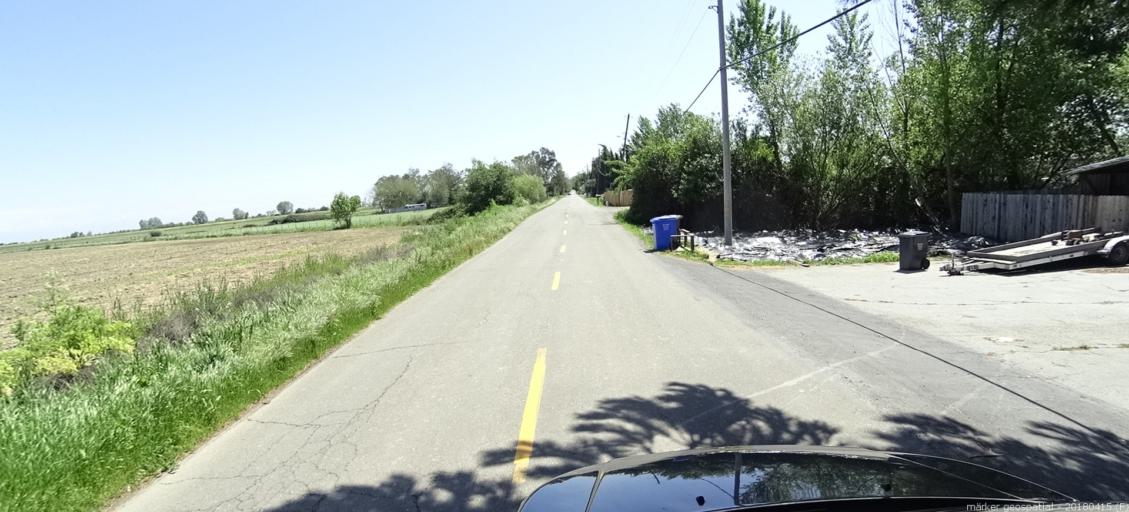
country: US
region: California
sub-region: Solano County
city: Rio Vista
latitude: 38.1660
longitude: -121.5940
